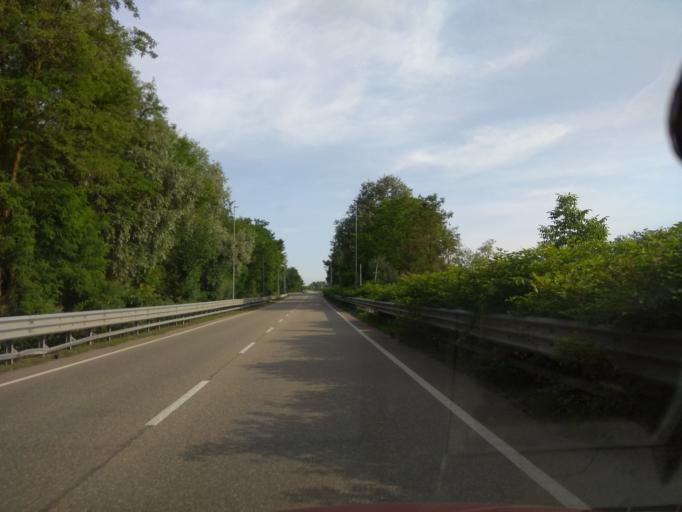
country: IT
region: Piedmont
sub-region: Provincia di Biella
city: Cerreto Castello
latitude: 45.5689
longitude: 8.1698
